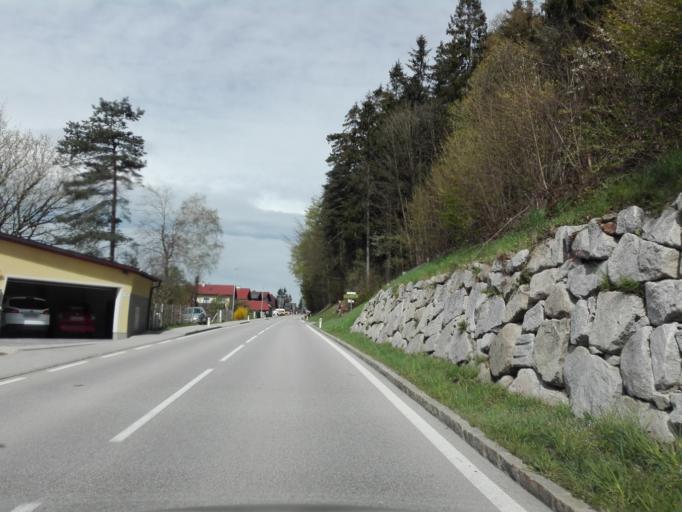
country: AT
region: Upper Austria
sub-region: Politischer Bezirk Urfahr-Umgebung
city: Eidenberg
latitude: 48.3471
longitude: 14.2437
